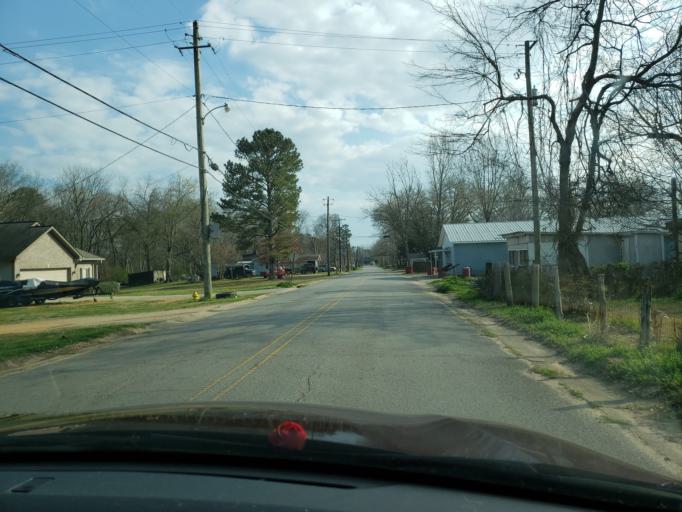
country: US
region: Alabama
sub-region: Hale County
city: Greensboro
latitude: 32.6985
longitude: -87.6094
